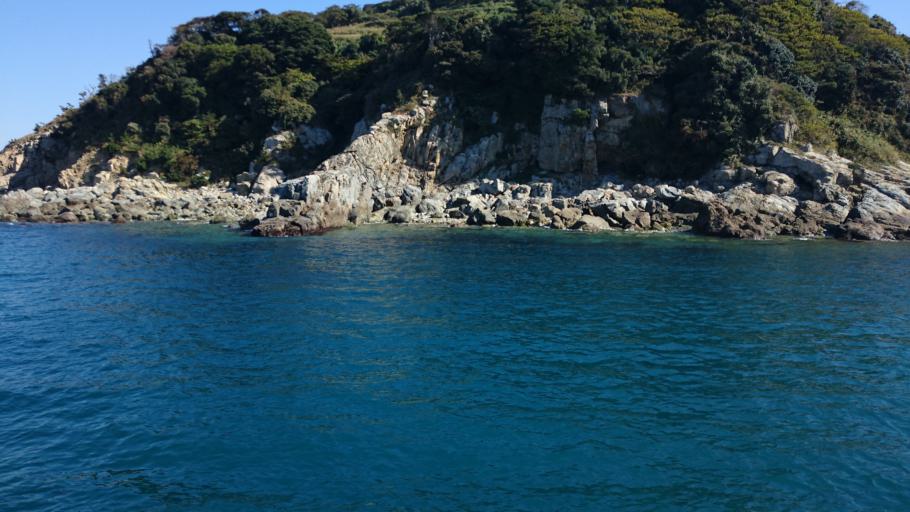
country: KR
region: Gyeongsangnam-do
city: Kyosai
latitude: 34.6496
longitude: 128.5743
